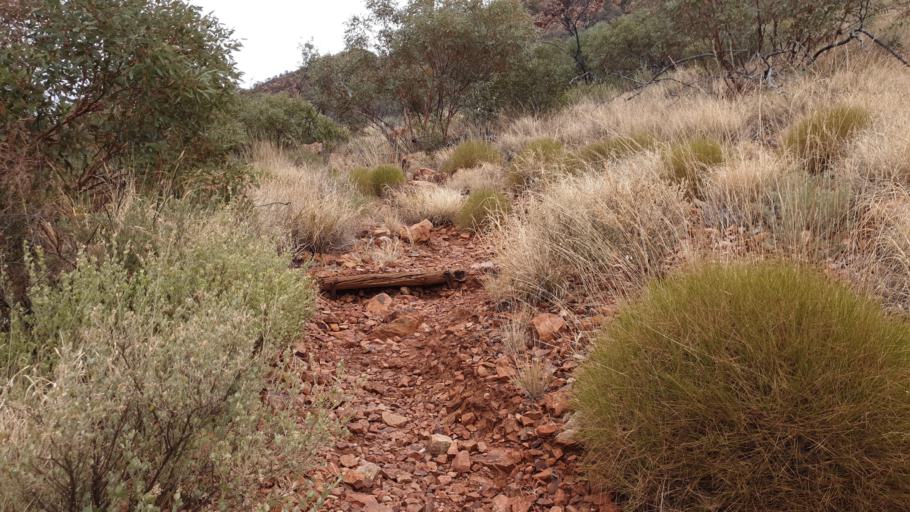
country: AU
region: Northern Territory
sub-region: Alice Springs
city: Alice Springs
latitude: -23.7790
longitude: 133.0710
